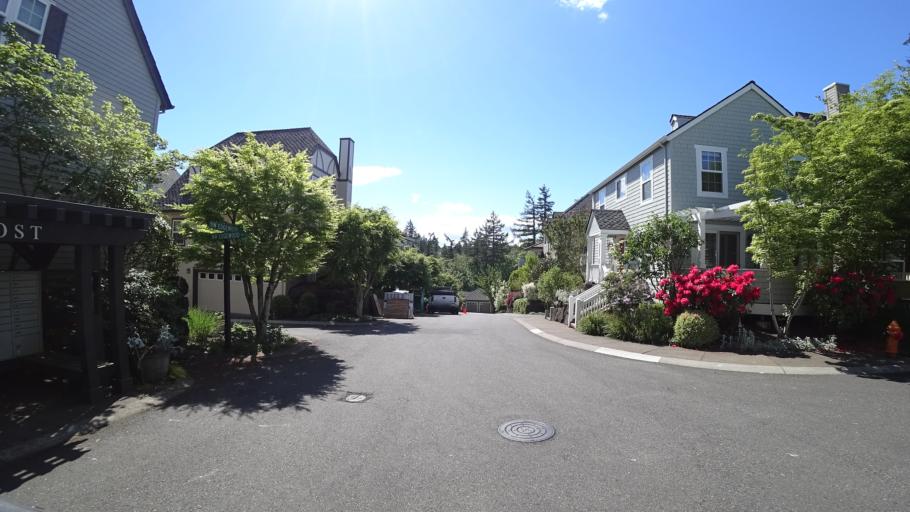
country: US
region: Oregon
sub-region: Washington County
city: West Haven
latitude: 45.5403
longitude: -122.7814
